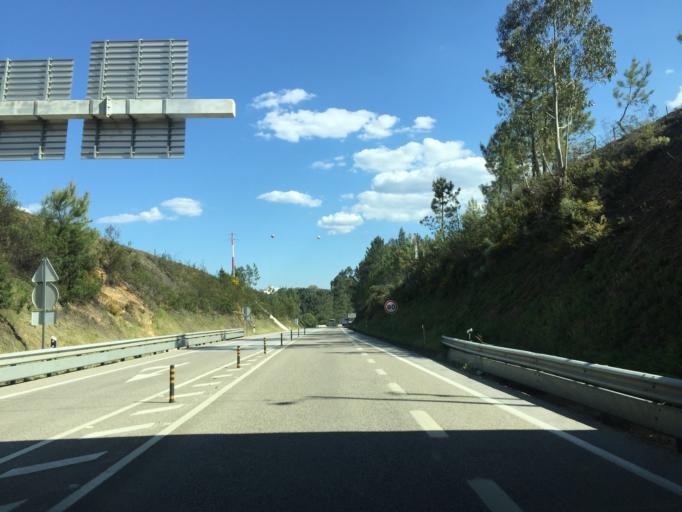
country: PT
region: Leiria
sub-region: Pedrogao Grande
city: Pedrogao Grande
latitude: 39.9224
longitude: -8.1558
